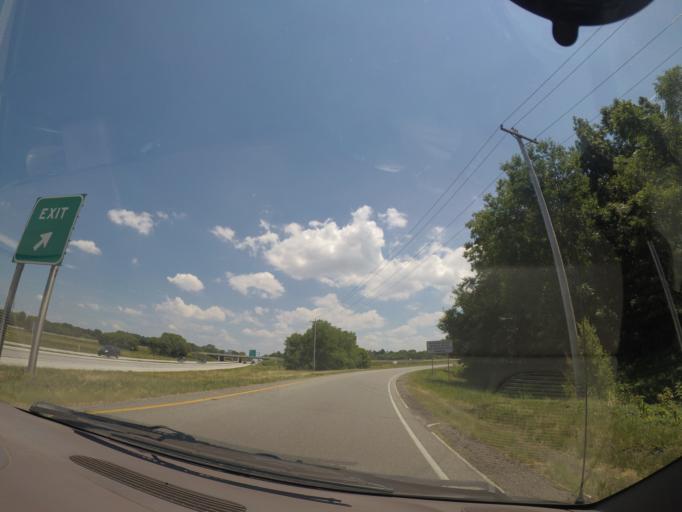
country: US
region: Indiana
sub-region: Saint Joseph County
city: South Bend
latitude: 41.6716
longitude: -86.3441
